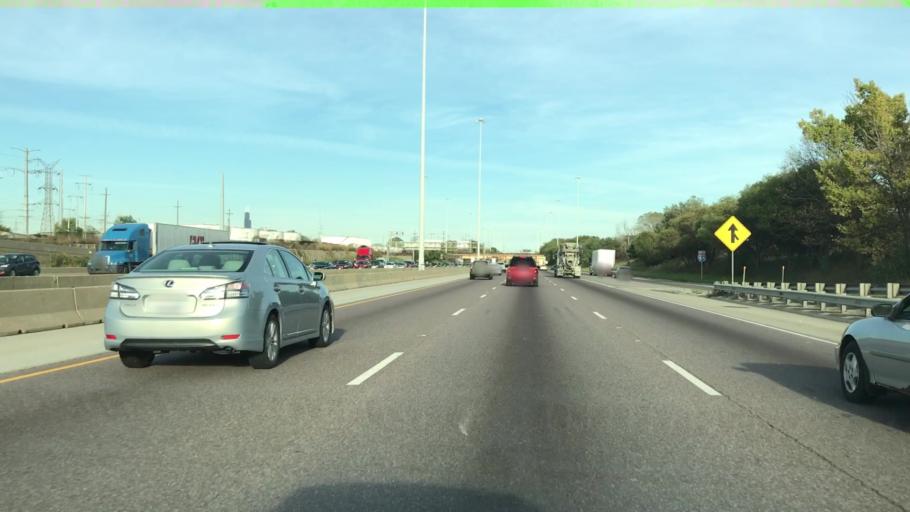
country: US
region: Illinois
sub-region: Cook County
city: Cicero
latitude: 41.8238
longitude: -87.7215
